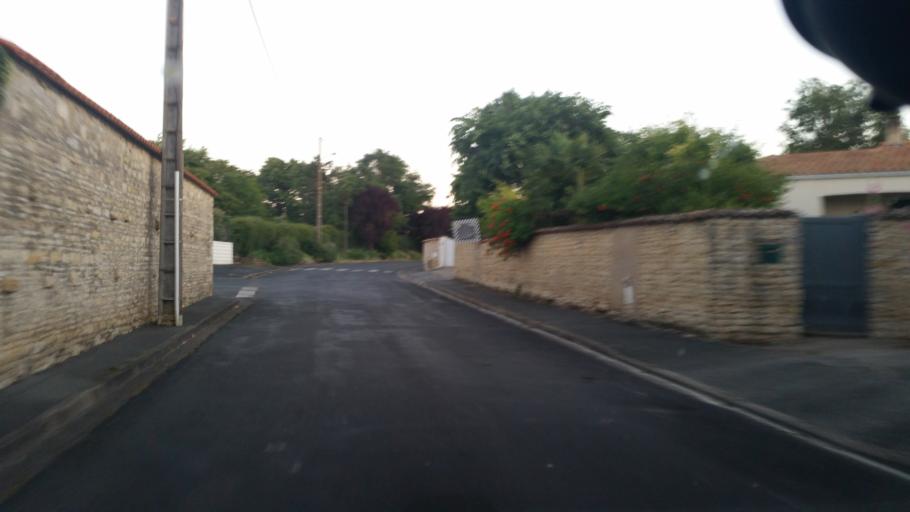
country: FR
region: Poitou-Charentes
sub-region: Departement de la Charente-Maritime
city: Marans
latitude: 46.3093
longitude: -0.9990
